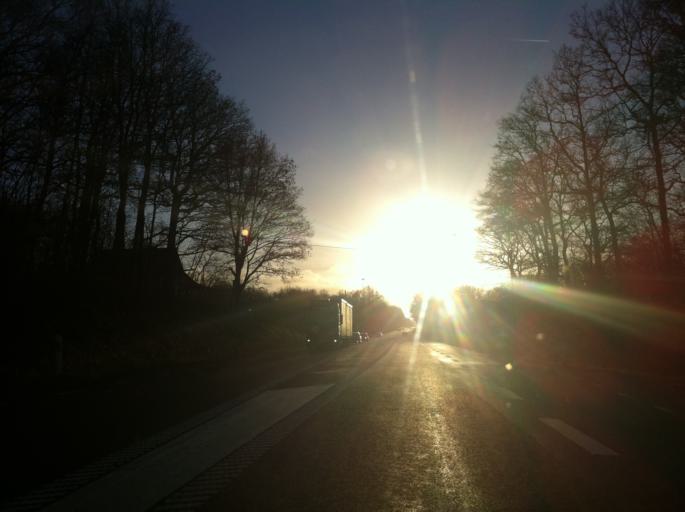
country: SE
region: Skane
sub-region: Hassleholms Kommun
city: Tormestorp
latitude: 56.0859
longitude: 13.7639
